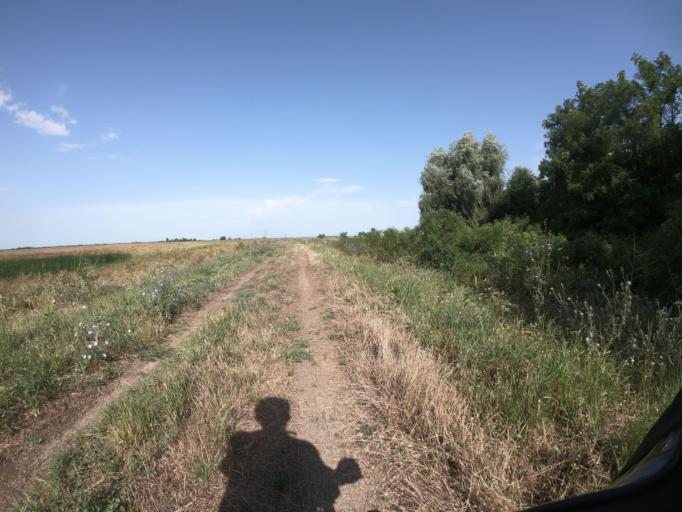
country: HU
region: Hajdu-Bihar
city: Egyek
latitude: 47.5786
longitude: 20.9233
